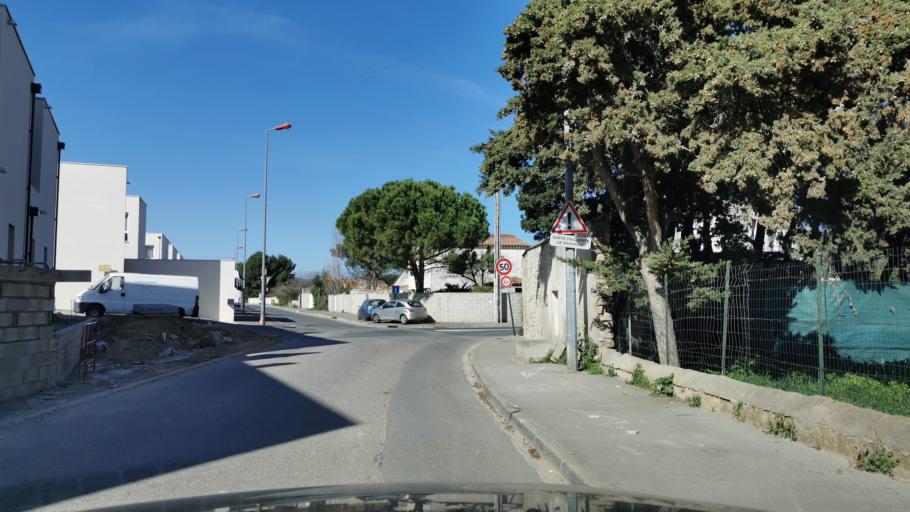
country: FR
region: Languedoc-Roussillon
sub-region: Departement de l'Aude
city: Narbonne
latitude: 43.1887
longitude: 2.9904
